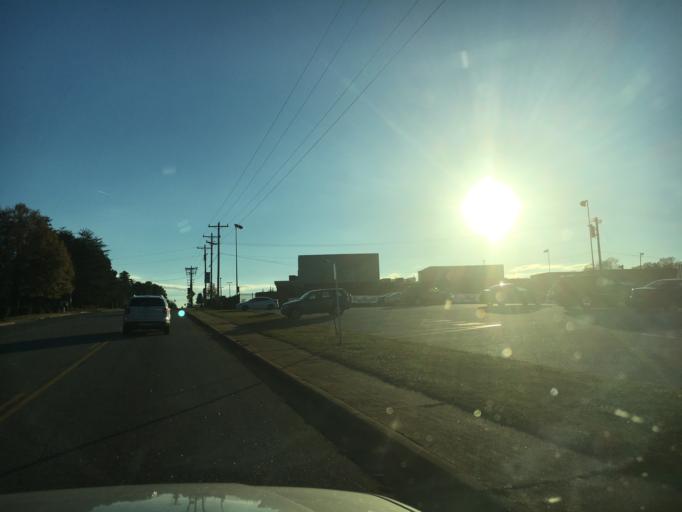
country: US
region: South Carolina
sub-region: Spartanburg County
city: Lyman
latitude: 34.9338
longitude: -82.1249
